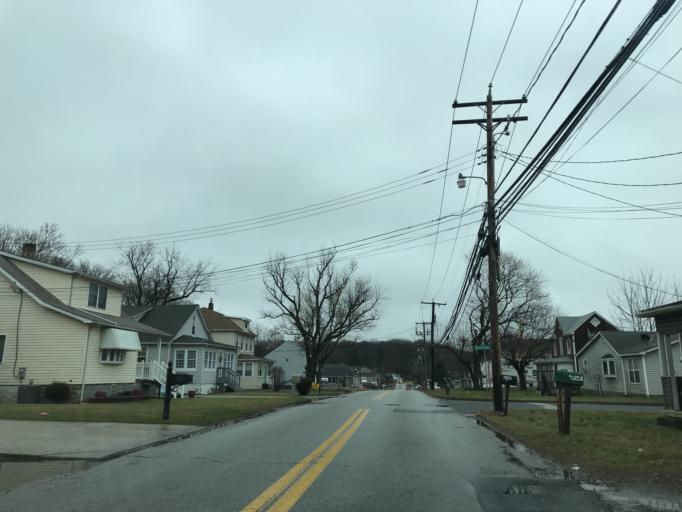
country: US
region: Maryland
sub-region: Baltimore County
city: Edgemere
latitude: 39.2315
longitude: -76.4501
